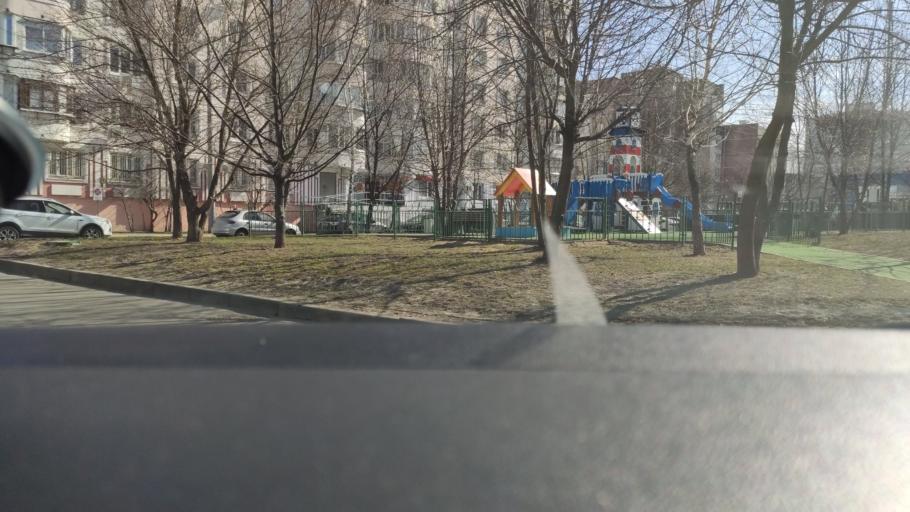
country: RU
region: Moskovskaya
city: Shcherbinka
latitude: 55.5380
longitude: 37.5300
